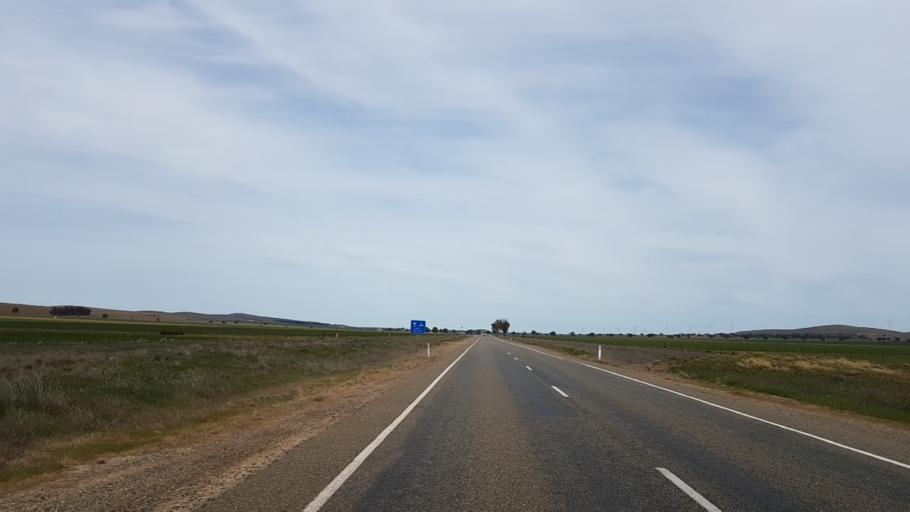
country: AU
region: South Australia
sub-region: Northern Areas
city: Jamestown
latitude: -33.0511
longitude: 138.6181
